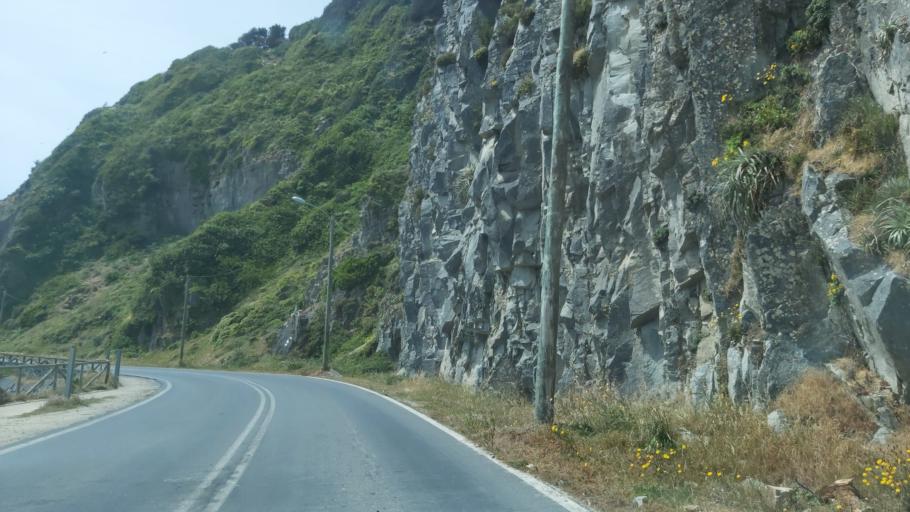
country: CL
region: Maule
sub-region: Provincia de Talca
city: Constitucion
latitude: -35.3326
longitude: -72.4337
